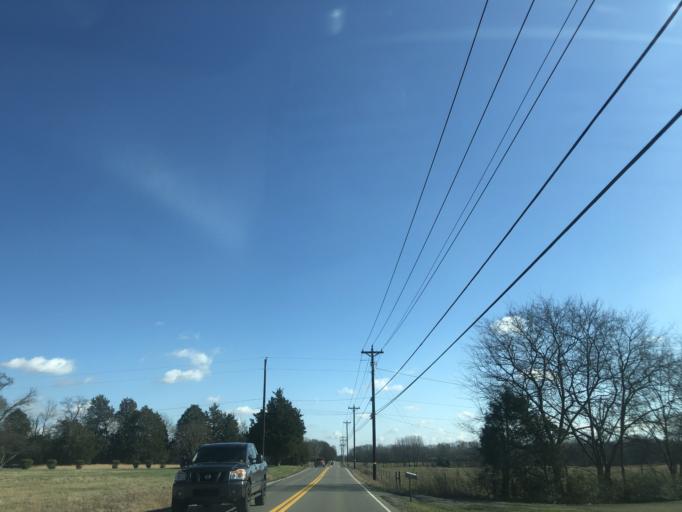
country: US
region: Tennessee
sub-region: Rutherford County
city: Smyrna
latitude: 35.9850
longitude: -86.4172
